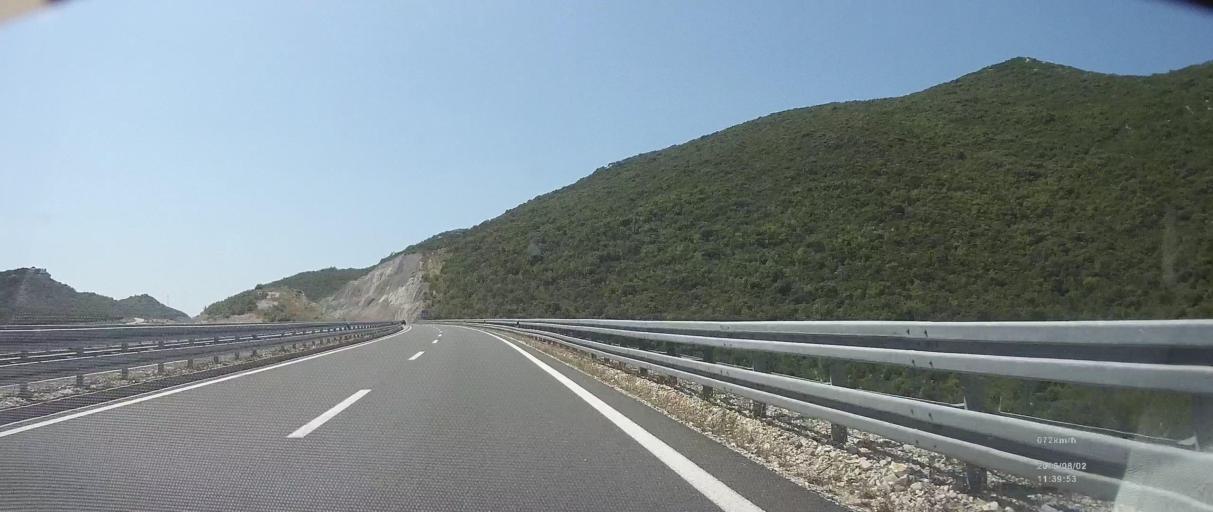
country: HR
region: Dubrovacko-Neretvanska
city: Komin
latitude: 43.0814
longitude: 17.4899
